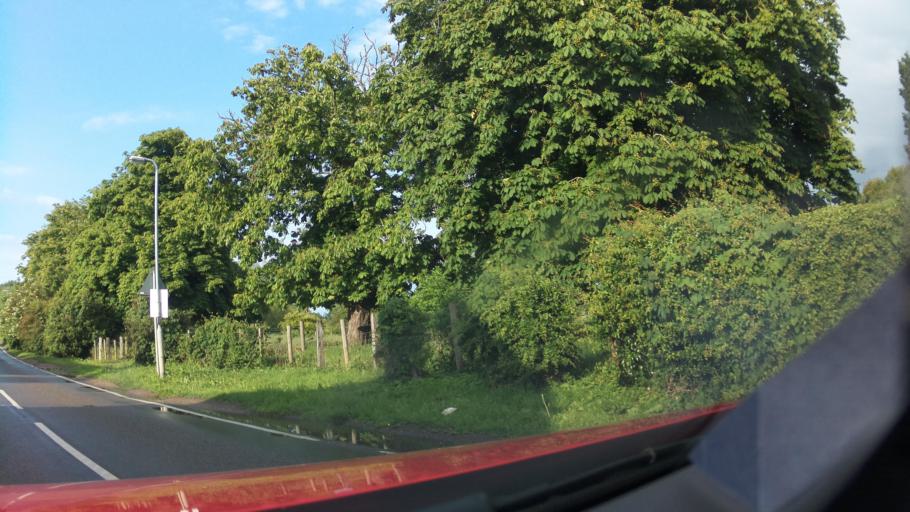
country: GB
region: England
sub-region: Lincolnshire
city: Great Gonerby
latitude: 52.9839
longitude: -0.6724
